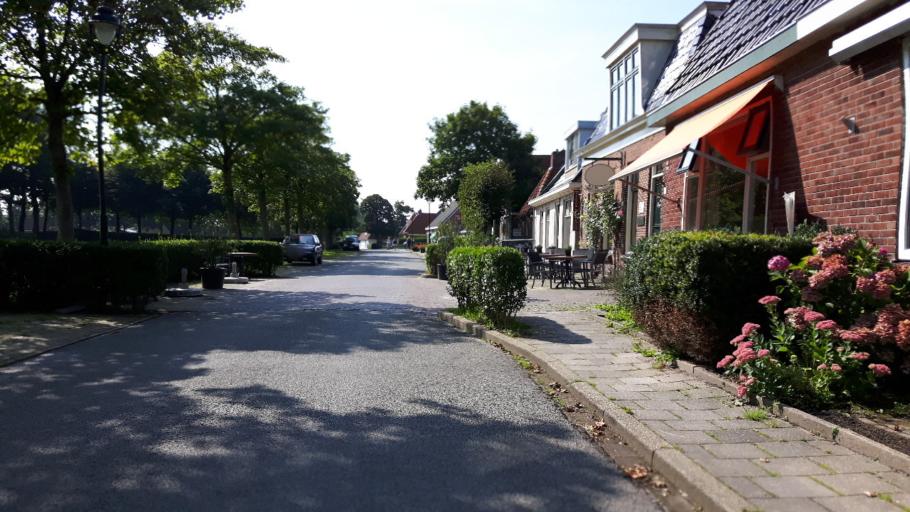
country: NL
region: Friesland
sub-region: Gemeente Ferwerderadiel
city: Hallum
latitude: 53.2928
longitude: 5.7670
